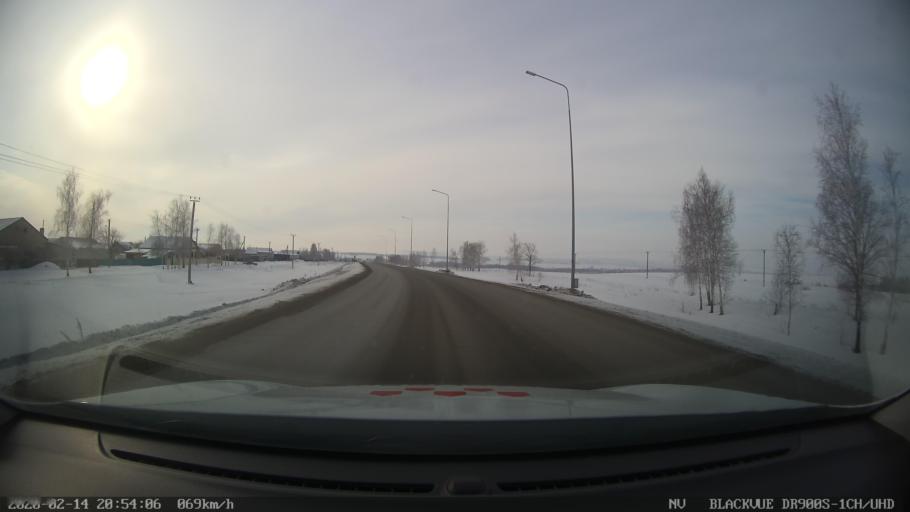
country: RU
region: Tatarstan
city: Kuybyshevskiy Zaton
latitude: 55.1890
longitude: 49.2456
